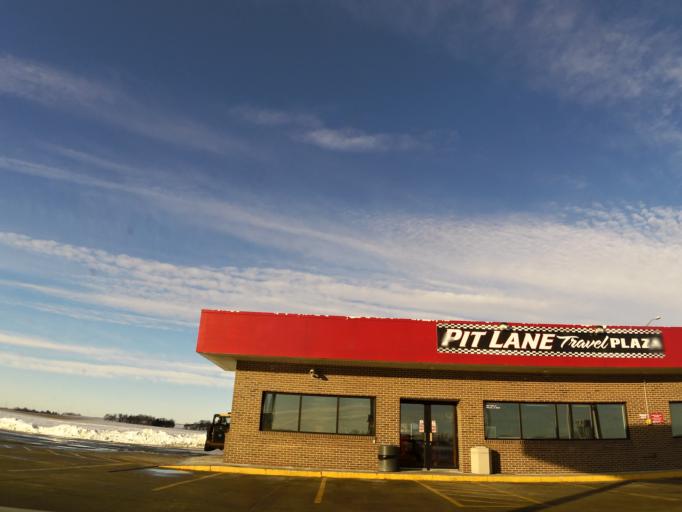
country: US
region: Iowa
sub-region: Butler County
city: Shell Rock
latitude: 42.7156
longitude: -92.5397
